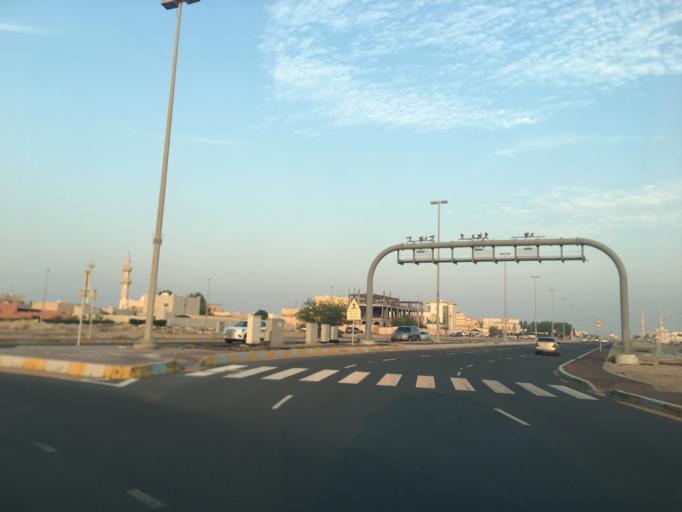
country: AE
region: Abu Dhabi
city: Abu Dhabi
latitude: 24.3064
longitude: 54.6395
